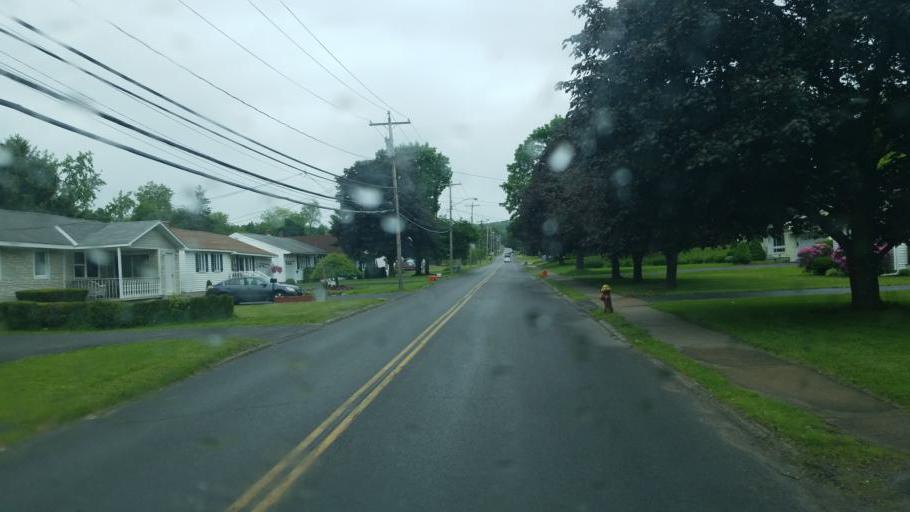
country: US
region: New York
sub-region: Oneida County
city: Utica
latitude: 43.1215
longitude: -75.2066
